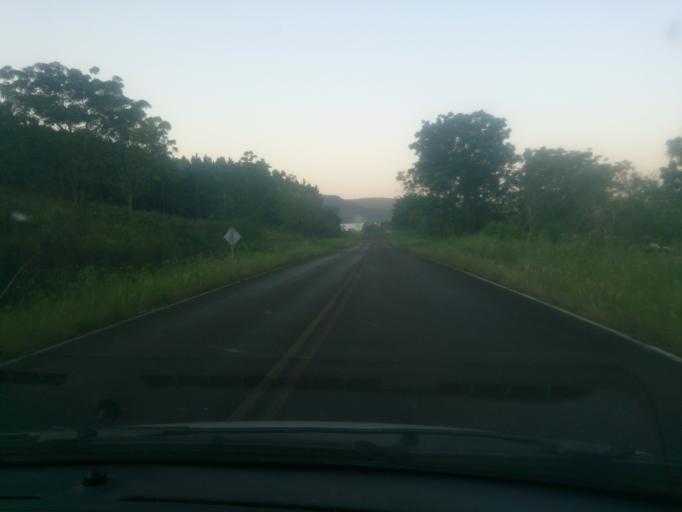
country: AR
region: Misiones
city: Panambi
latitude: -27.6585
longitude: -54.9089
